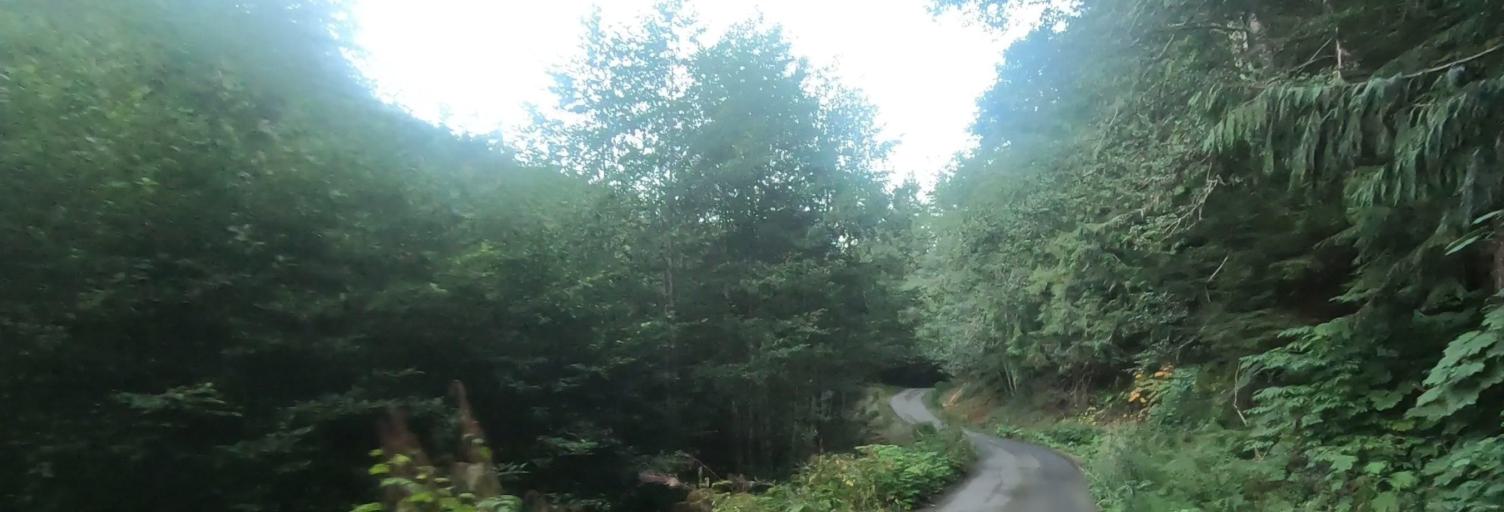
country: US
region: Washington
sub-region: Whatcom County
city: Peaceful Valley
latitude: 48.9466
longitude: -121.9388
